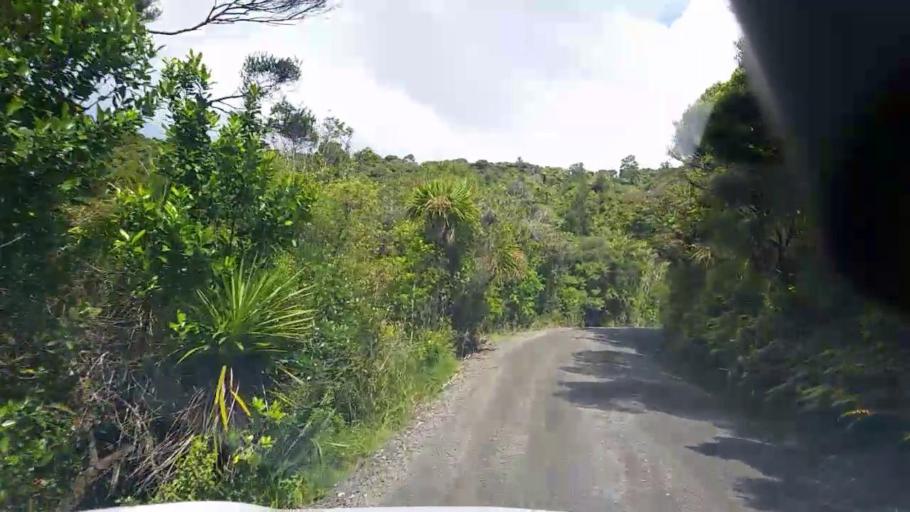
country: NZ
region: Auckland
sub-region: Auckland
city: Muriwai Beach
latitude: -36.9258
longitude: 174.4812
